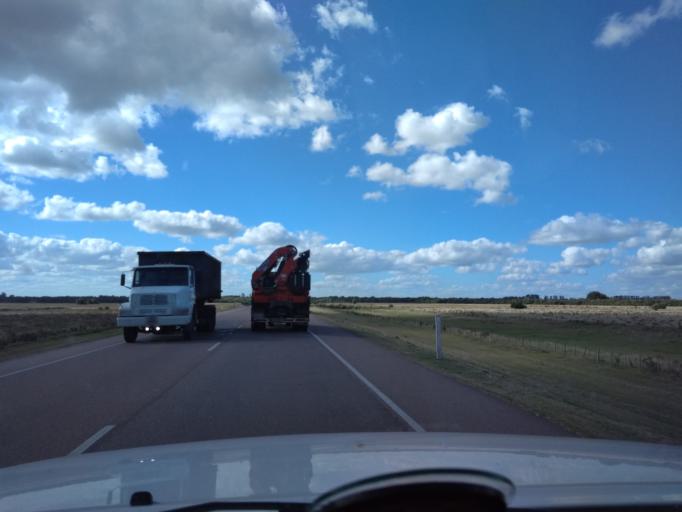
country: UY
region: Canelones
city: Canelones
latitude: -34.3754
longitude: -56.2516
